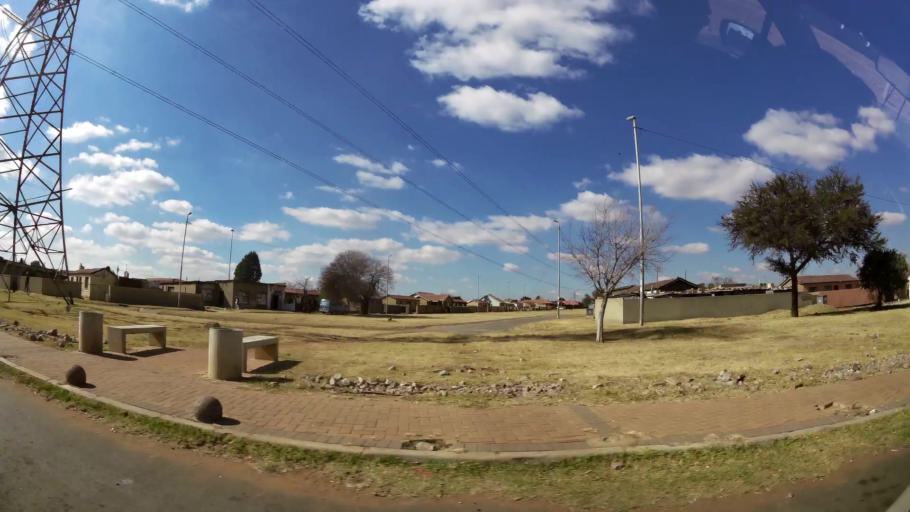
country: ZA
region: Gauteng
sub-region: West Rand District Municipality
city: Krugersdorp
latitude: -26.1415
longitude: 27.7933
